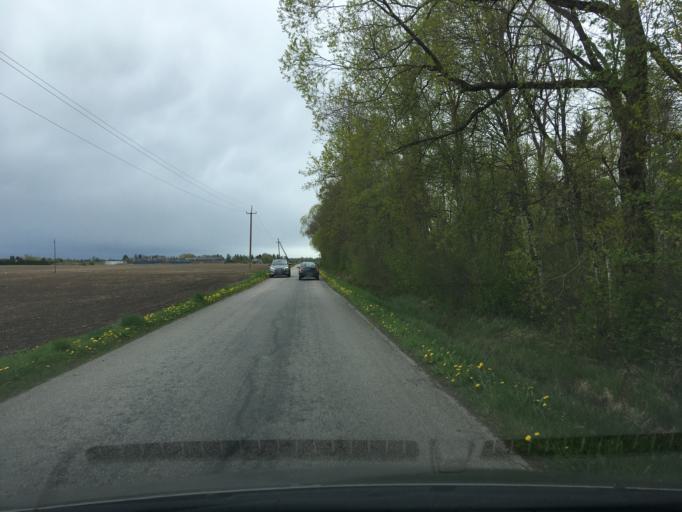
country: EE
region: Harju
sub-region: Joelaehtme vald
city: Loo
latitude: 59.3743
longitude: 24.9660
